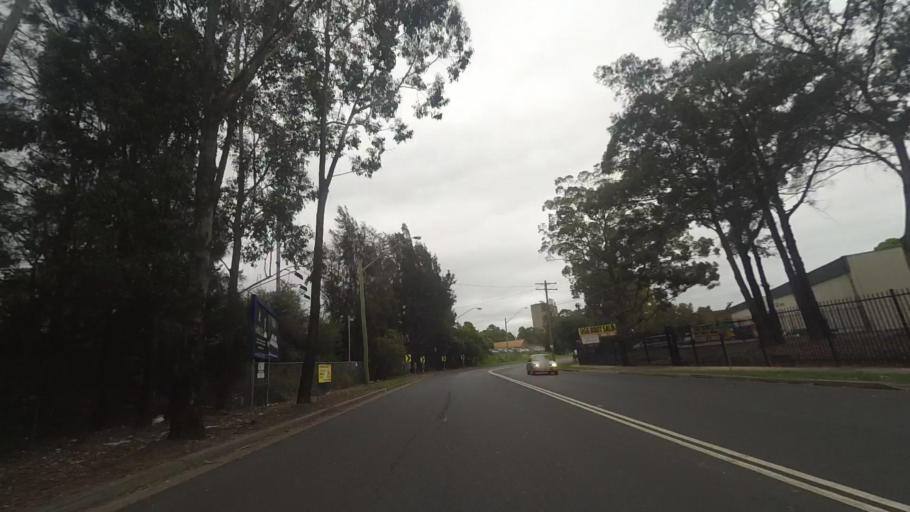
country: AU
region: New South Wales
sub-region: Auburn
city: Auburn
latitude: -33.8419
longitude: 151.0265
